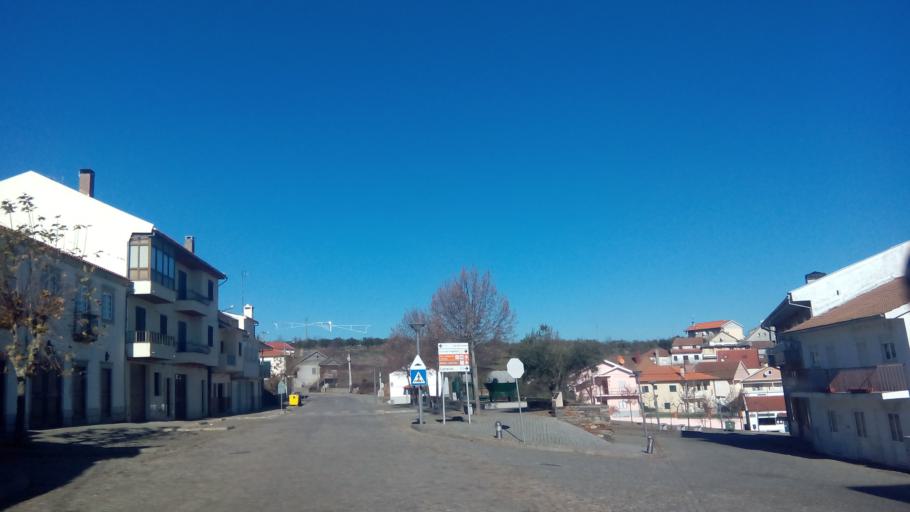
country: PT
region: Braganca
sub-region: Vimioso
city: Vimioso
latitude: 41.6444
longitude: -6.6008
